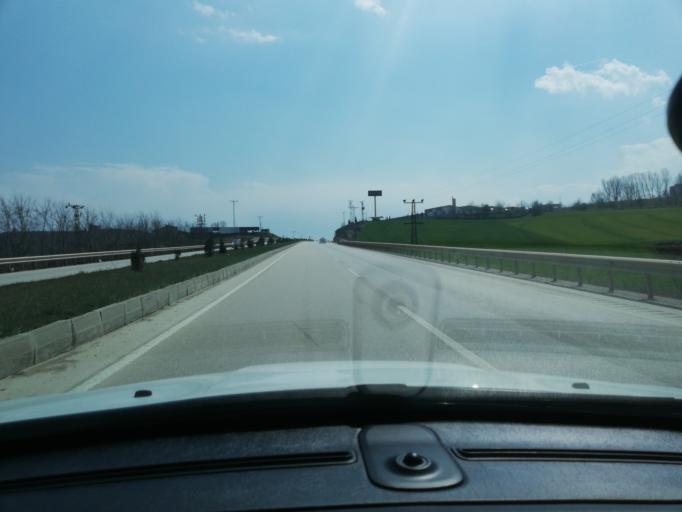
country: TR
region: Kastamonu
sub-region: Cide
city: Kastamonu
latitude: 41.4400
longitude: 33.7969
